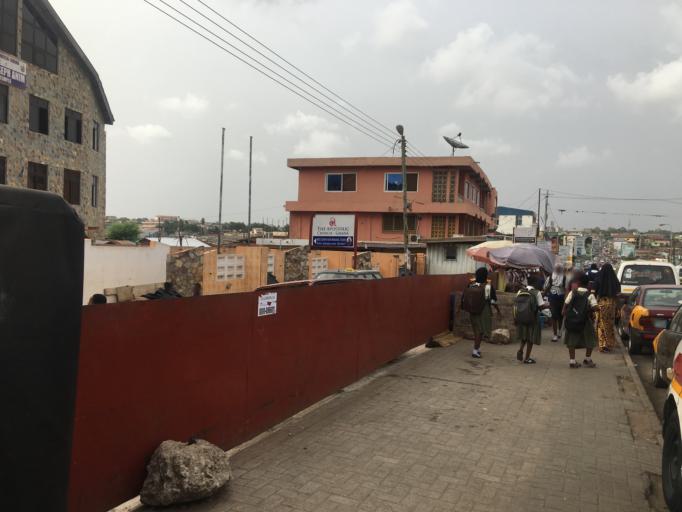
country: GH
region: Greater Accra
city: Accra
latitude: 5.5861
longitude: -0.1973
